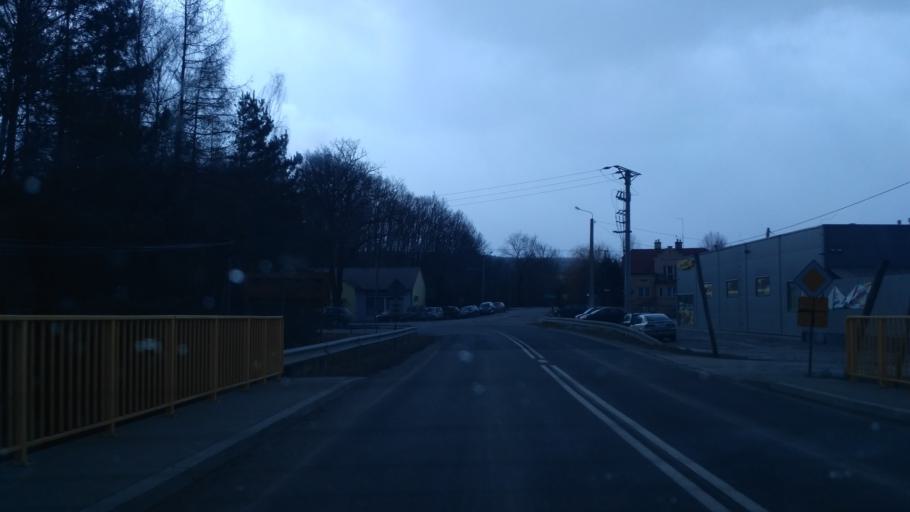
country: PL
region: Subcarpathian Voivodeship
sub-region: Powiat rzeszowski
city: Hyzne
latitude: 49.9102
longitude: 22.1995
